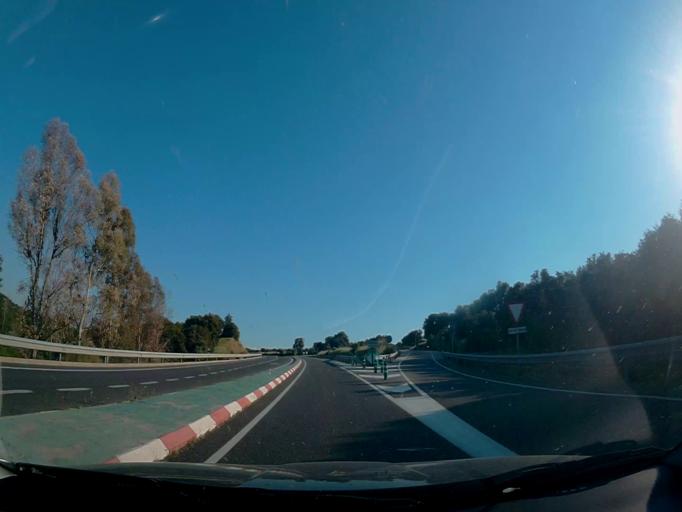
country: ES
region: Castille-La Mancha
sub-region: Province of Toledo
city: Escalona
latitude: 40.1905
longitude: -4.4041
